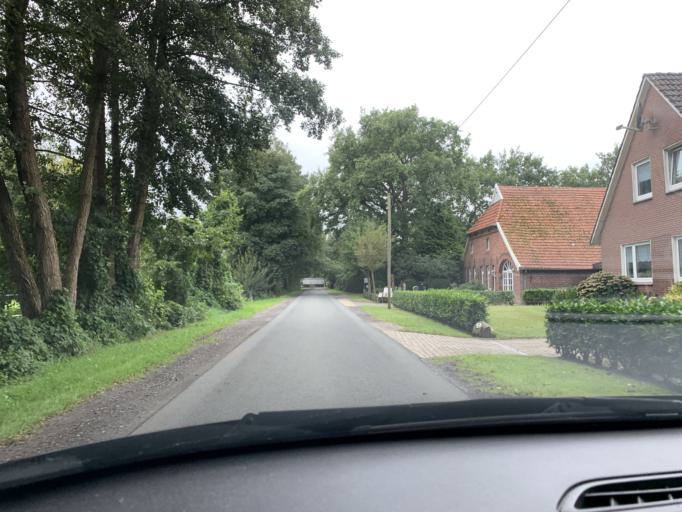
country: DE
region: Lower Saxony
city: Westerstede
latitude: 53.2792
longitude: 7.8884
